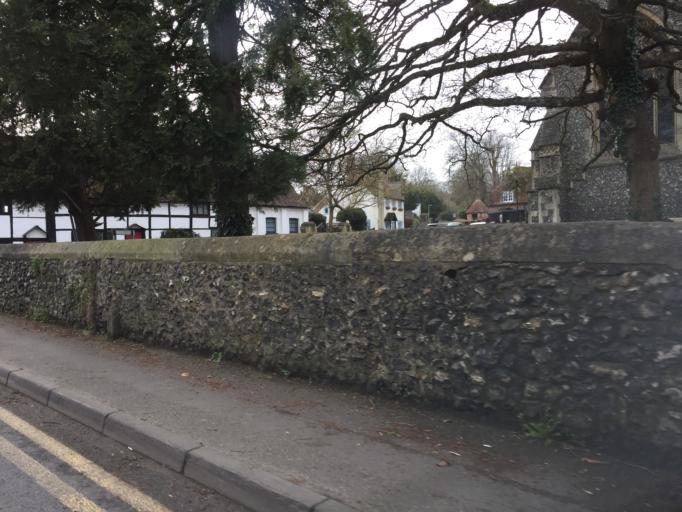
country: GB
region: England
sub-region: West Berkshire
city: Pangbourne
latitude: 51.4833
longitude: -1.0875
